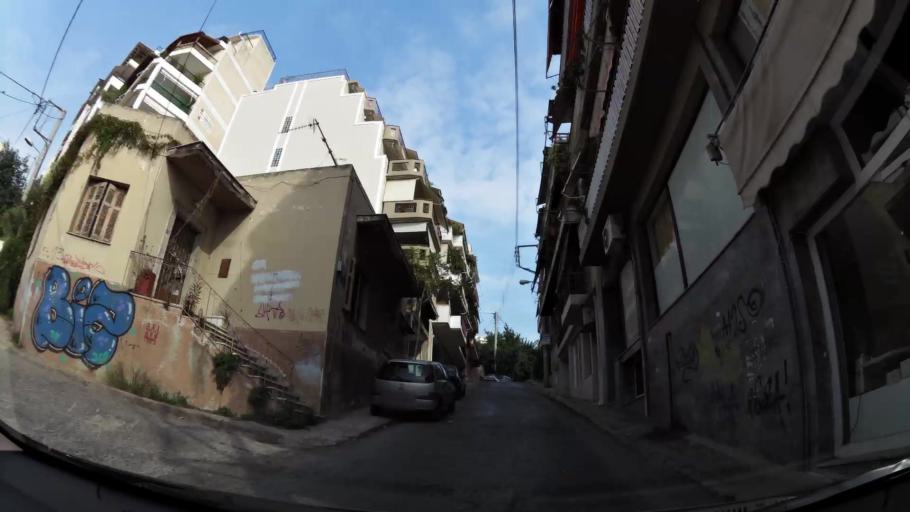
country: GR
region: Attica
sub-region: Nomarchia Athinas
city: Kipseli
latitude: 37.9929
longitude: 23.7535
